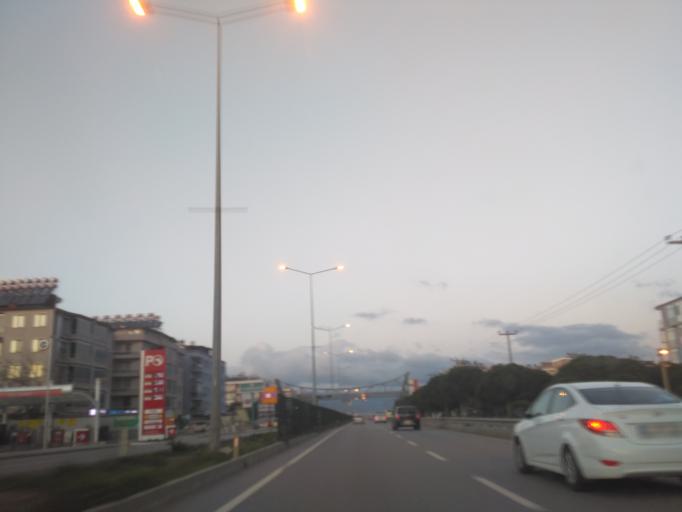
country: TR
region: Balikesir
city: Burhaniye
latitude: 39.5057
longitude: 26.9709
